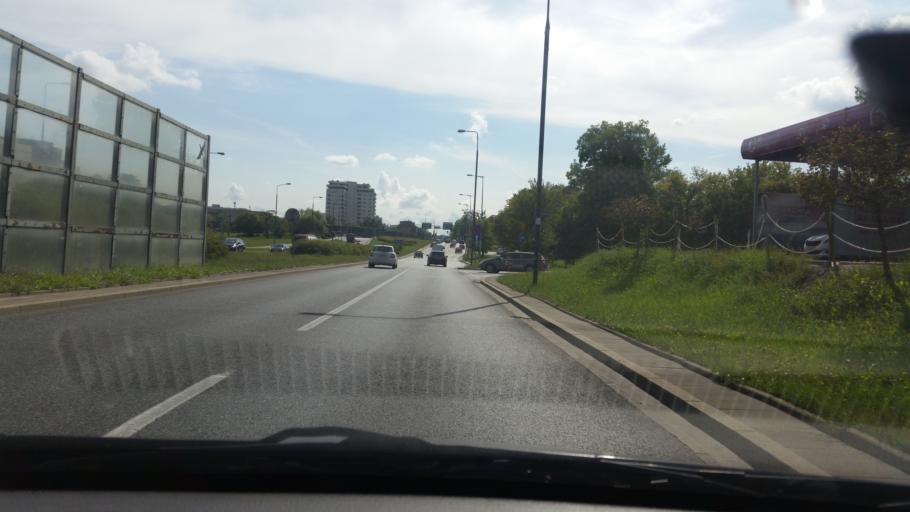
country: PL
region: Masovian Voivodeship
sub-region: Warszawa
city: Bielany
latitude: 52.2639
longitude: 20.9489
